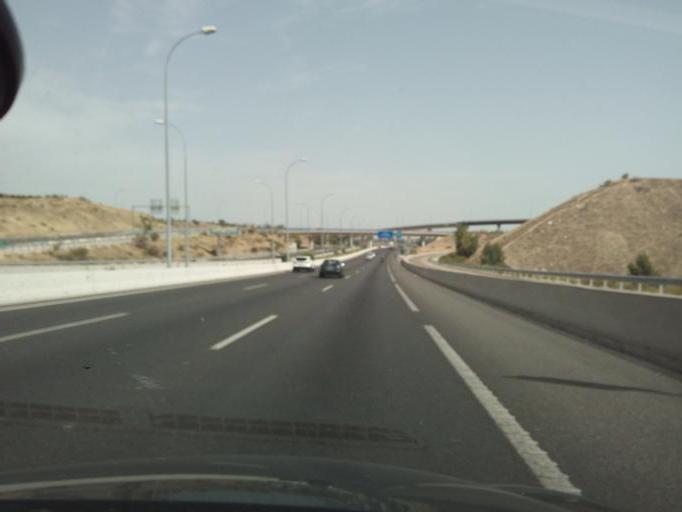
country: ES
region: Madrid
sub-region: Provincia de Madrid
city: Hortaleza
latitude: 40.4927
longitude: -3.6451
